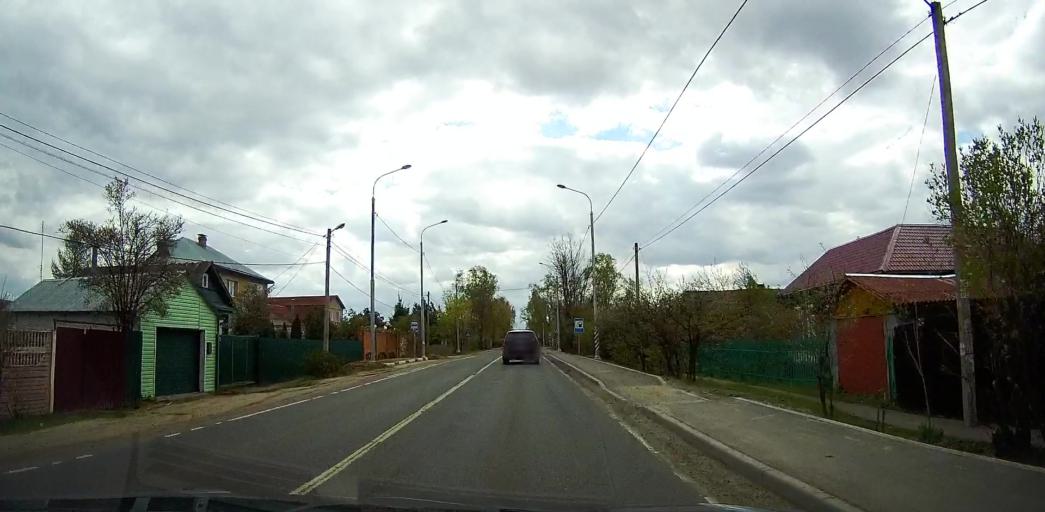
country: RU
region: Moskovskaya
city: Beloozerskiy
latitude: 55.4625
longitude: 38.4213
